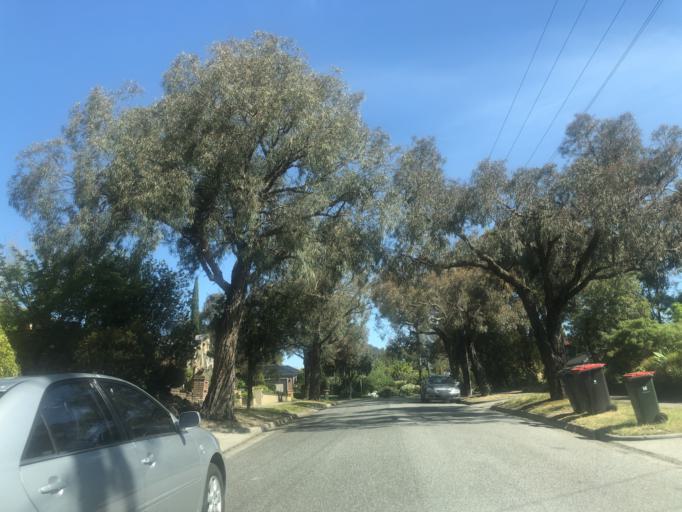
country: AU
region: Victoria
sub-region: Monash
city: Mulgrave
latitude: -37.8998
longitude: 145.1880
